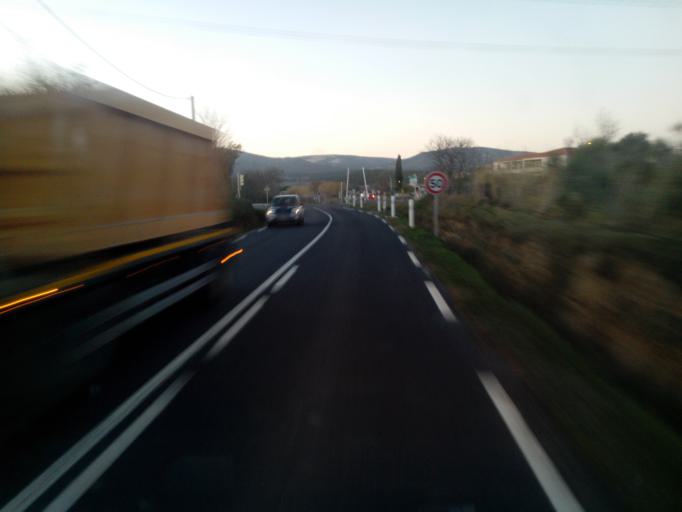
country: FR
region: Languedoc-Roussillon
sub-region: Departement des Pyrenees-Orientales
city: Peyrestortes
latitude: 42.7723
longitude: 2.8321
